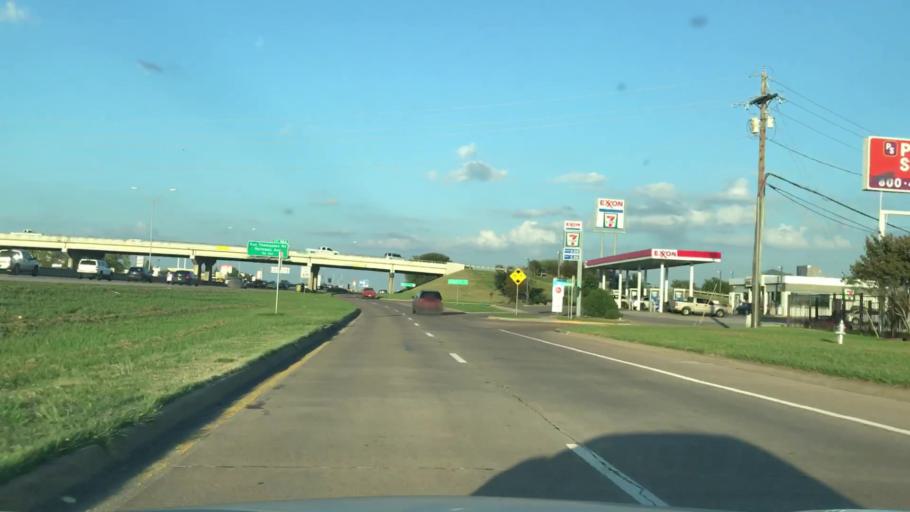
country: US
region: Texas
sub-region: Dallas County
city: Mesquite
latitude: 32.8091
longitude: -96.6562
